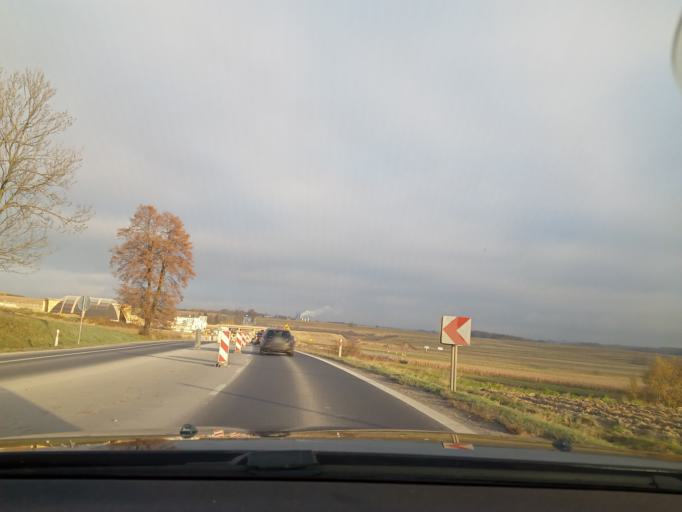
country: PL
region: Lesser Poland Voivodeship
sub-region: Powiat miechowski
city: Miechow
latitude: 50.3108
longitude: 20.0402
